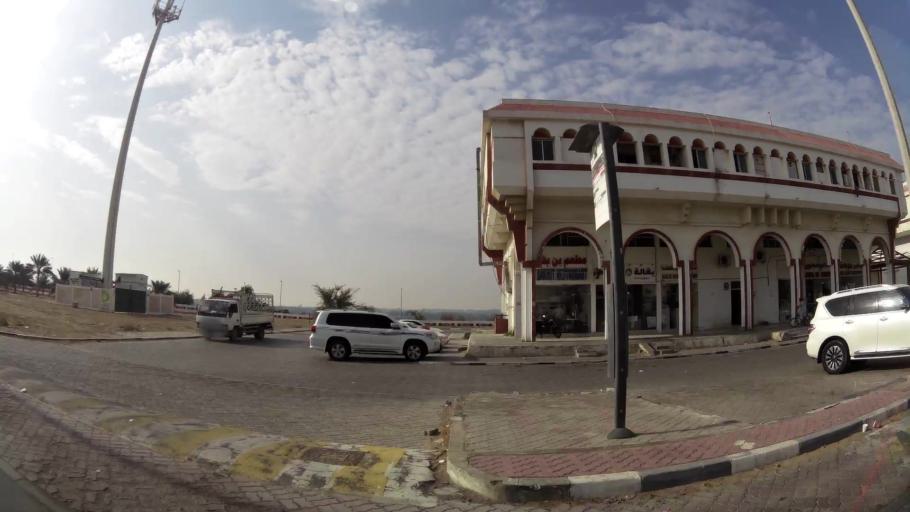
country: AE
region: Abu Dhabi
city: Abu Dhabi
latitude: 24.2396
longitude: 54.7181
